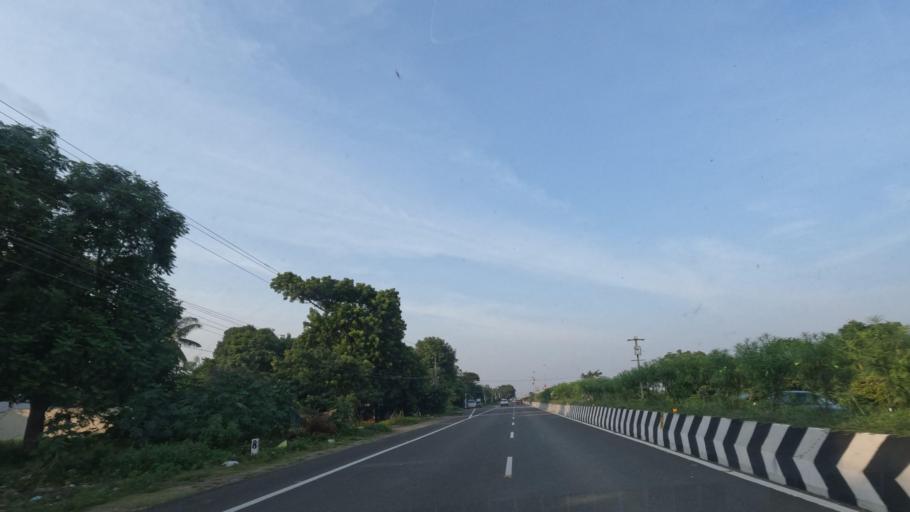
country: IN
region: Tamil Nadu
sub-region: Kancheepuram
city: Mamallapuram
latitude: 12.6854
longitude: 80.2156
